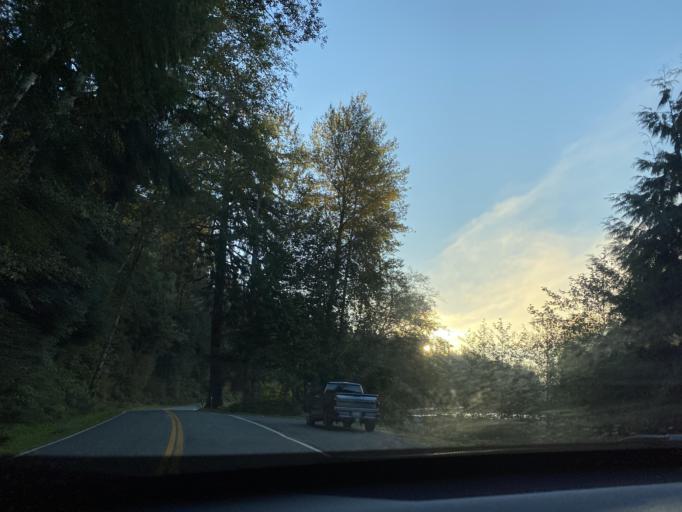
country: US
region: Washington
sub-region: Clallam County
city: Forks
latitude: 47.8229
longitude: -124.1917
